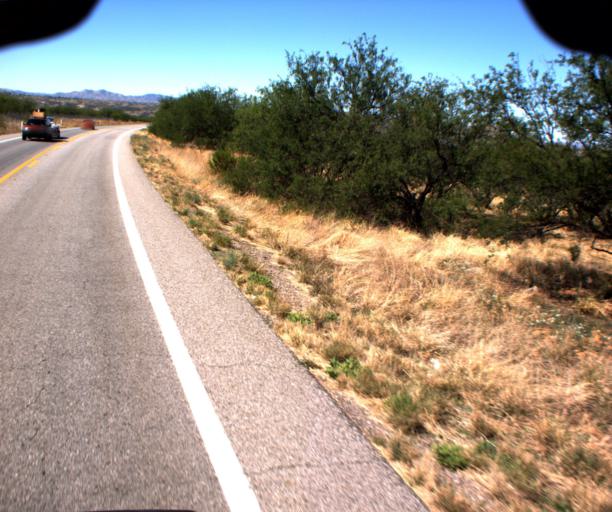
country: US
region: Arizona
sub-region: Santa Cruz County
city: Nogales
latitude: 31.4137
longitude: -110.8559
